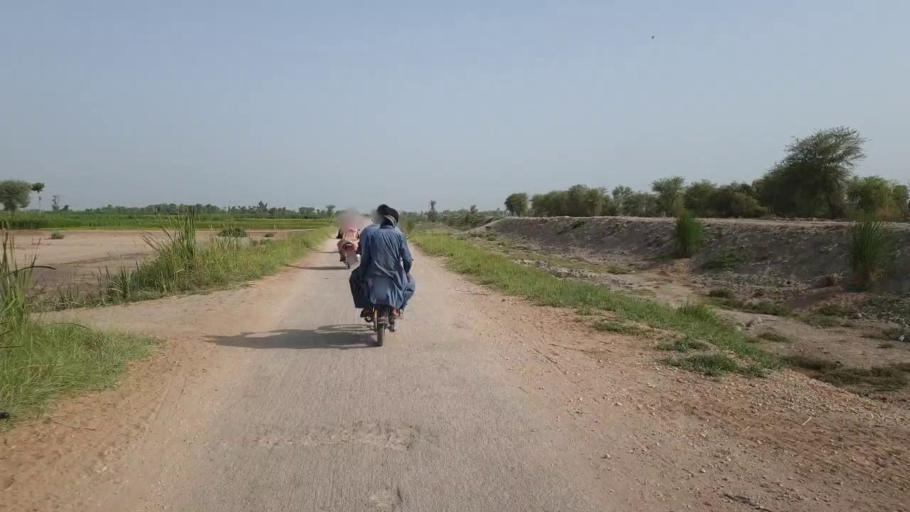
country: PK
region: Sindh
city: Daur
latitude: 26.3513
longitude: 68.1615
